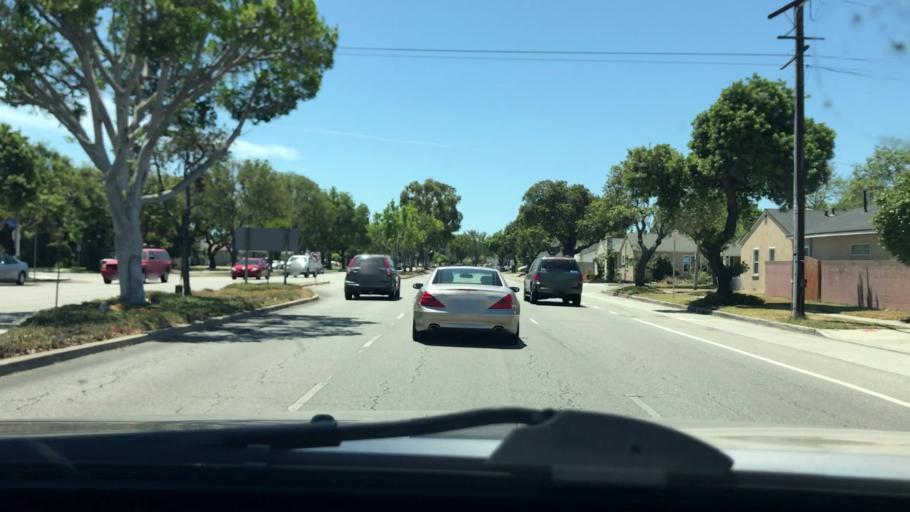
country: US
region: California
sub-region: Orange County
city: Rossmoor
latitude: 33.7937
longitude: -118.1254
